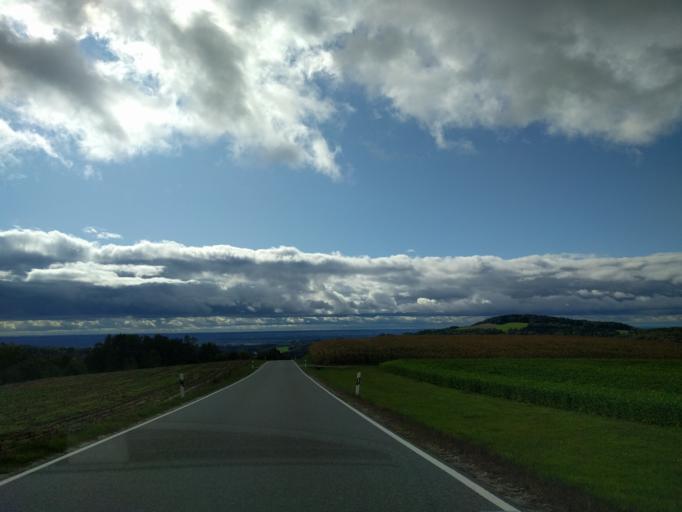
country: DE
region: Bavaria
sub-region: Lower Bavaria
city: Schaufling
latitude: 48.8238
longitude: 13.0537
